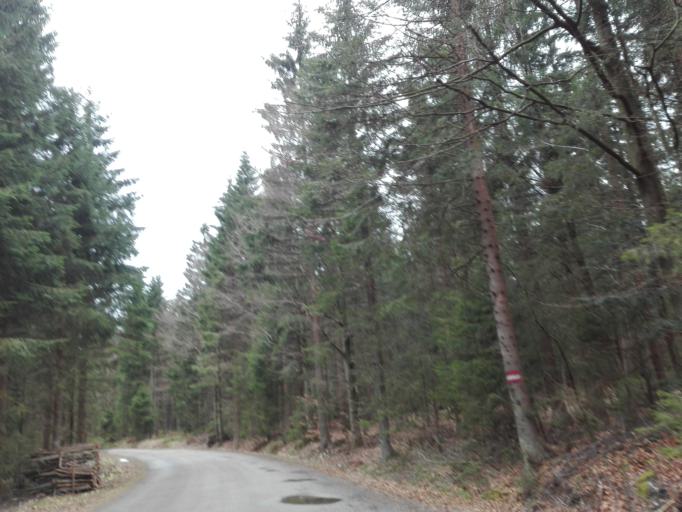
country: AT
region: Upper Austria
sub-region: Politischer Bezirk Rohrbach
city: Aigen im Muehlkreis
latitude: 48.6972
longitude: 13.9677
